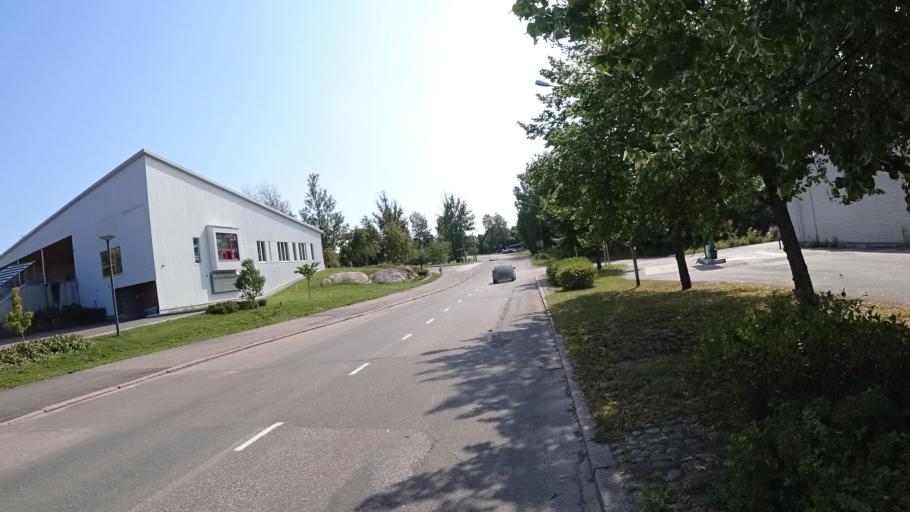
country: FI
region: Kymenlaakso
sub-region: Kotka-Hamina
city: Kotka
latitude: 60.4557
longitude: 26.9368
